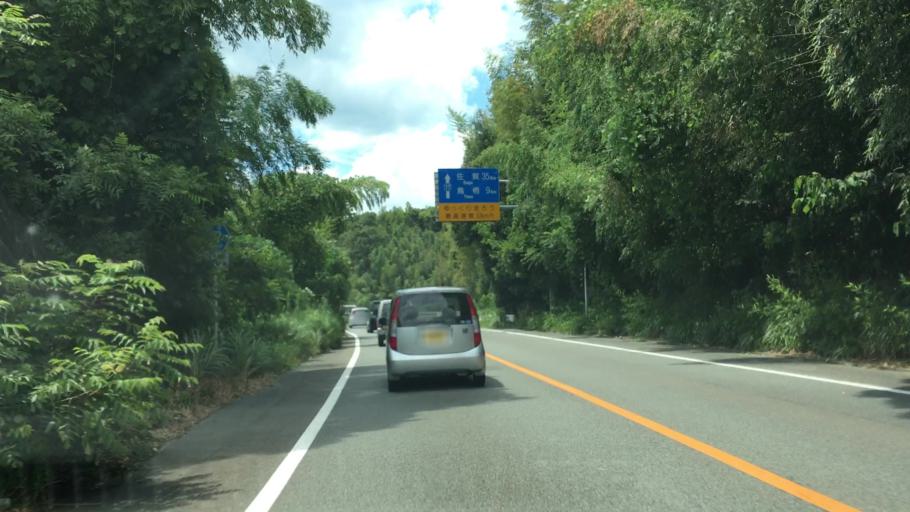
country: JP
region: Fukuoka
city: Chikushino-shi
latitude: 33.4444
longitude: 130.5328
